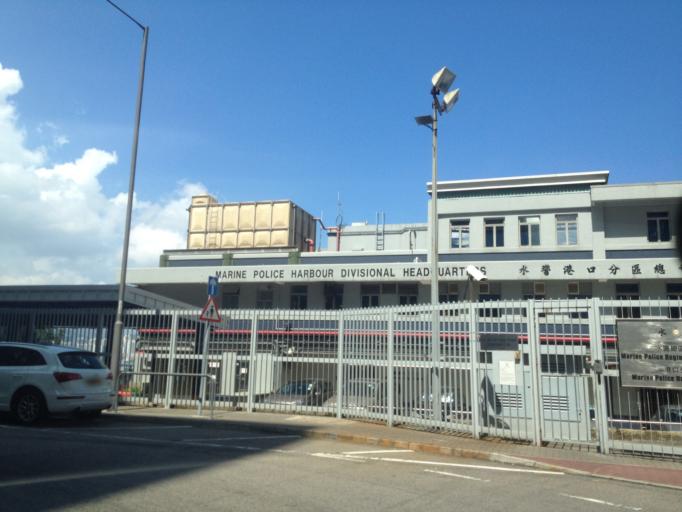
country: HK
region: Kowloon City
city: Kowloon
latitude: 22.2857
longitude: 114.2245
